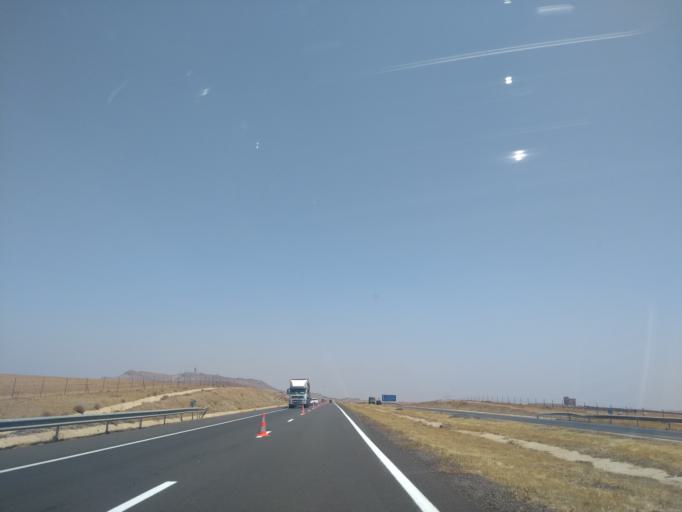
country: MA
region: Marrakech-Tensift-Al Haouz
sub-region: Kelaa-Des-Sraghna
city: Sidi Abdallah
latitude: 32.4434
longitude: -7.9318
